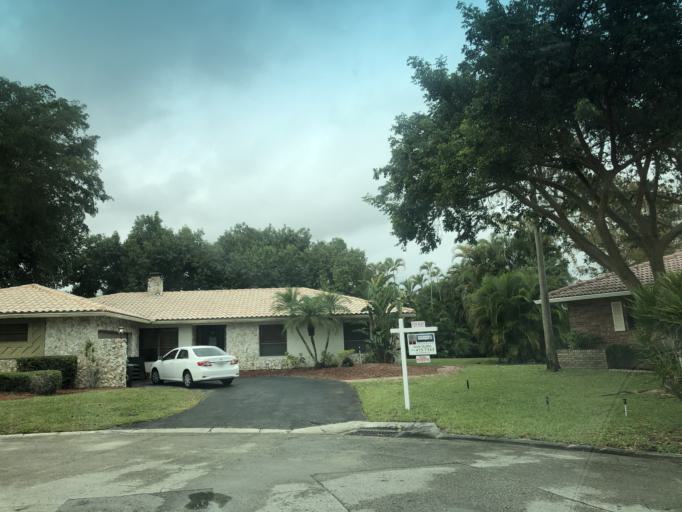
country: US
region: Florida
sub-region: Broward County
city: North Lauderdale
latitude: 26.2319
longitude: -80.2379
